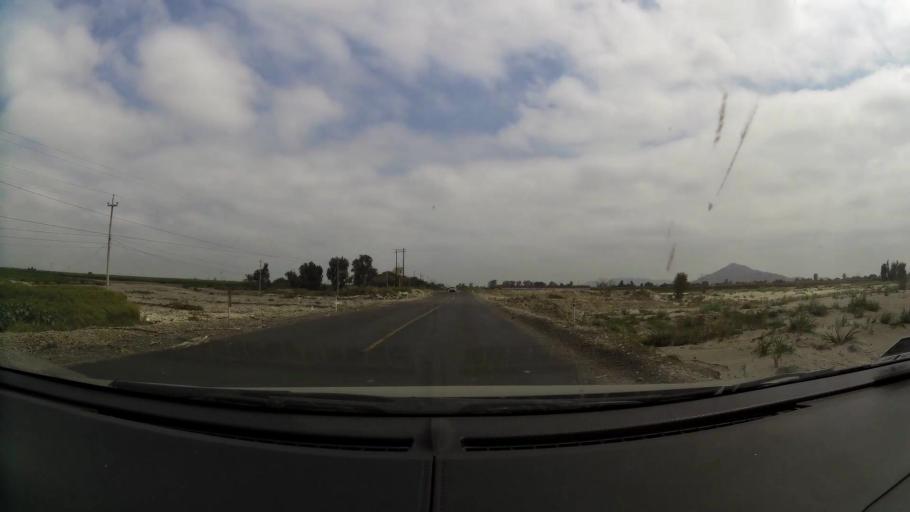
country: PE
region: La Libertad
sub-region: Ascope
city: Chicama
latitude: -7.8133
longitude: -79.1807
